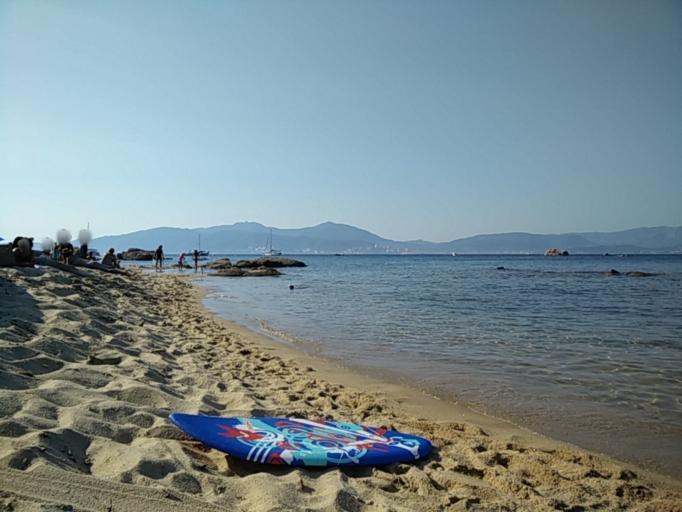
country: FR
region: Corsica
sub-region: Departement de la Corse-du-Sud
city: Pietrosella
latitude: 41.8468
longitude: 8.7668
